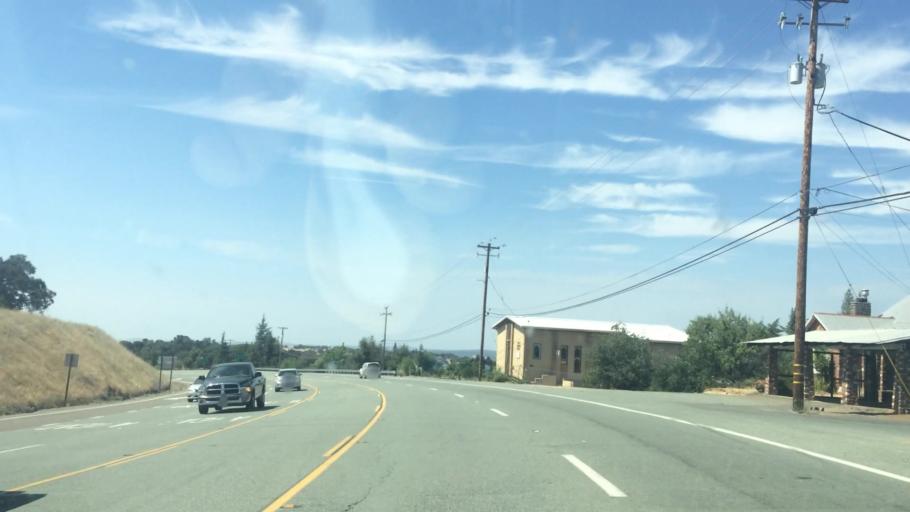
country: US
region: California
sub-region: Amador County
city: Sutter Creek
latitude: 38.3795
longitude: -120.8028
